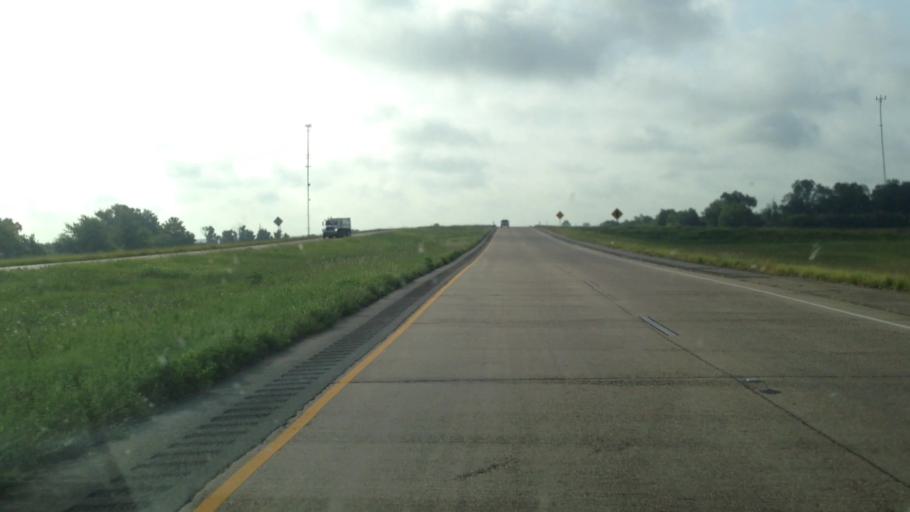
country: US
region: Louisiana
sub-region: Rapides Parish
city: Lecompte
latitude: 31.0159
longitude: -92.3799
